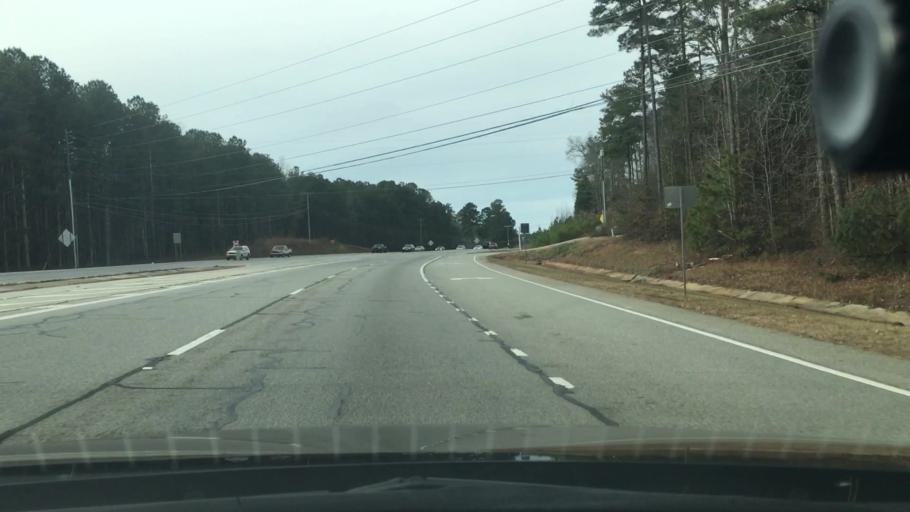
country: US
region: Georgia
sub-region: Fayette County
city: Peachtree City
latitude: 33.4001
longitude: -84.6597
